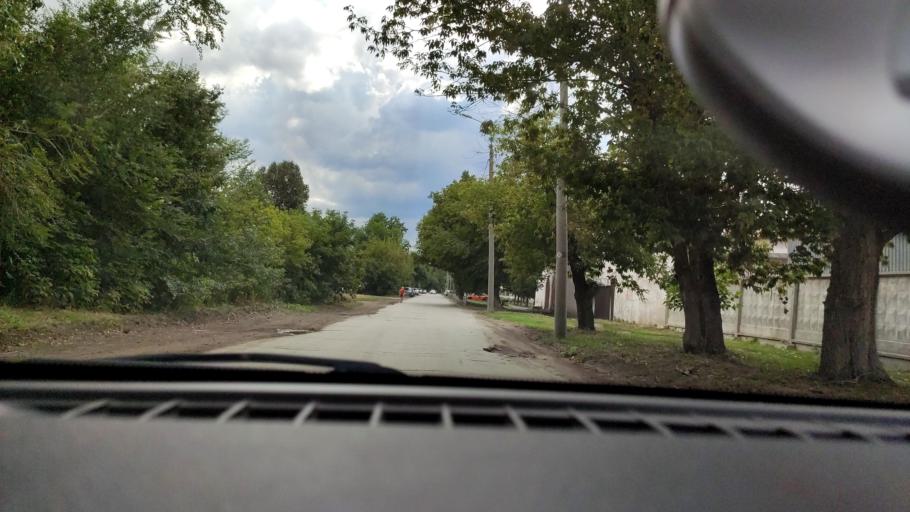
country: RU
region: Samara
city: Novokuybyshevsk
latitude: 53.1062
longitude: 50.0404
